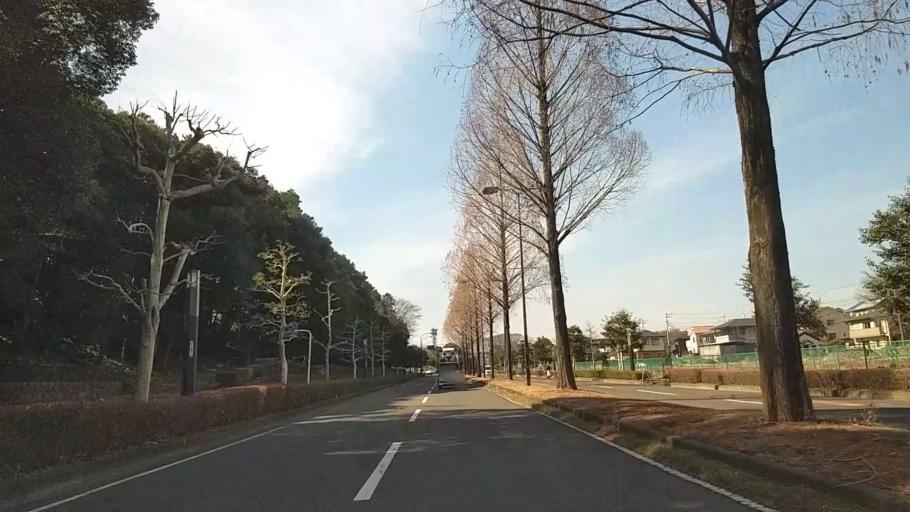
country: JP
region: Kanagawa
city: Fujisawa
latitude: 35.3915
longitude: 139.4273
